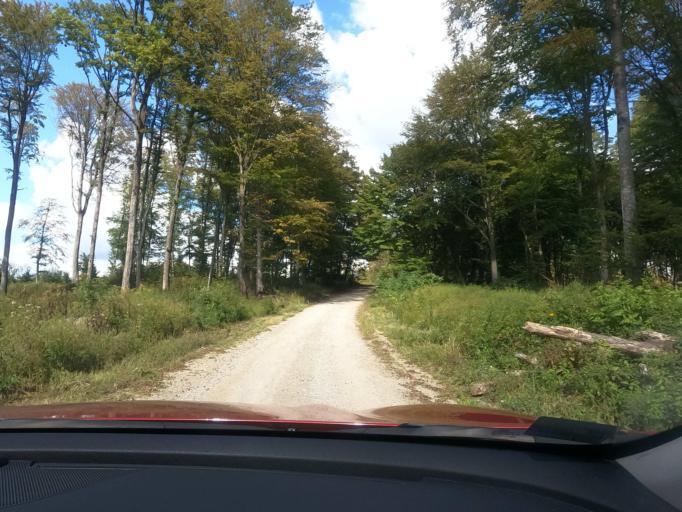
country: HR
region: Karlovacka
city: Vojnic
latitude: 45.2859
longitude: 15.7798
